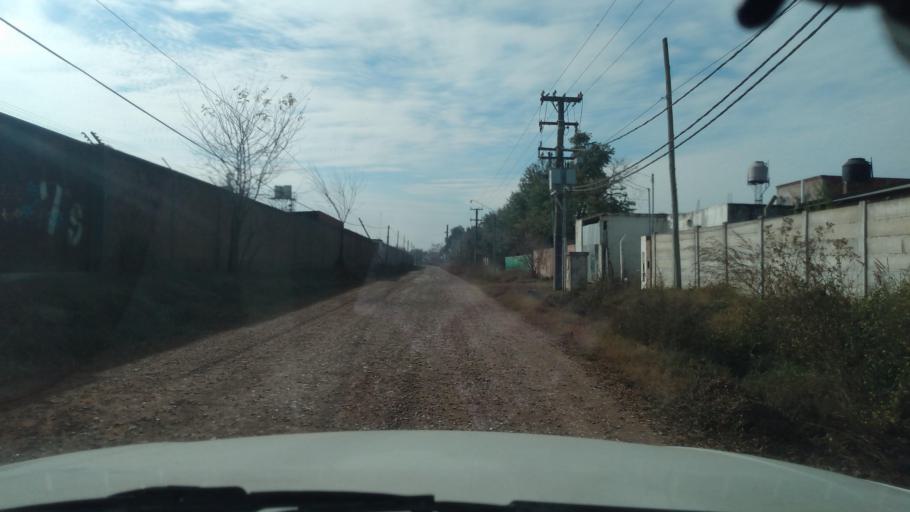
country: AR
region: Buenos Aires
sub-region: Partido de Lujan
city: Lujan
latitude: -34.5857
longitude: -59.1205
